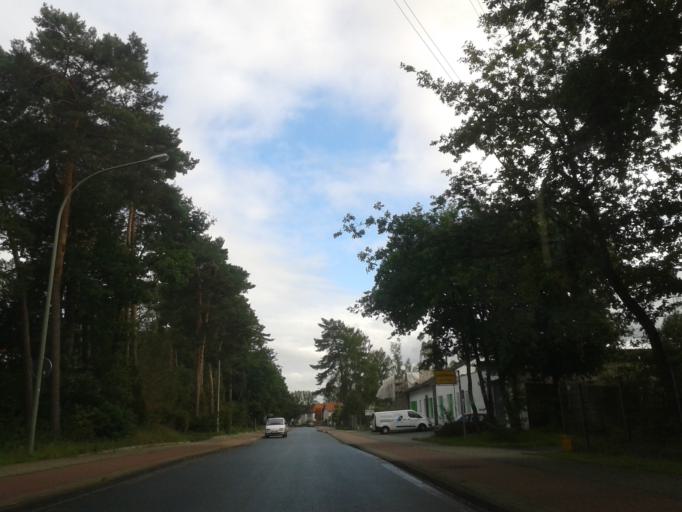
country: DE
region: North Rhine-Westphalia
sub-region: Regierungsbezirk Detmold
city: Paderborn
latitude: 51.7568
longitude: 8.7020
